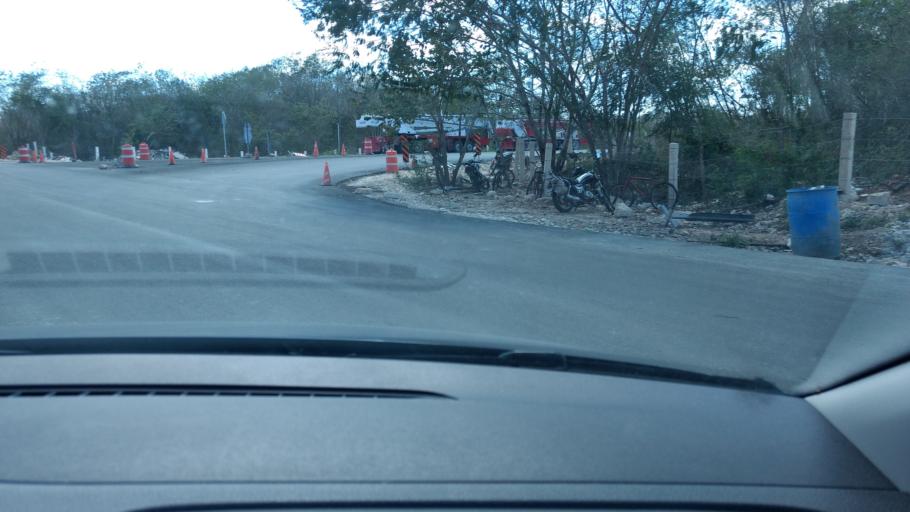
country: MX
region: Yucatan
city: Peto
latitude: 20.1193
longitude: -88.9478
